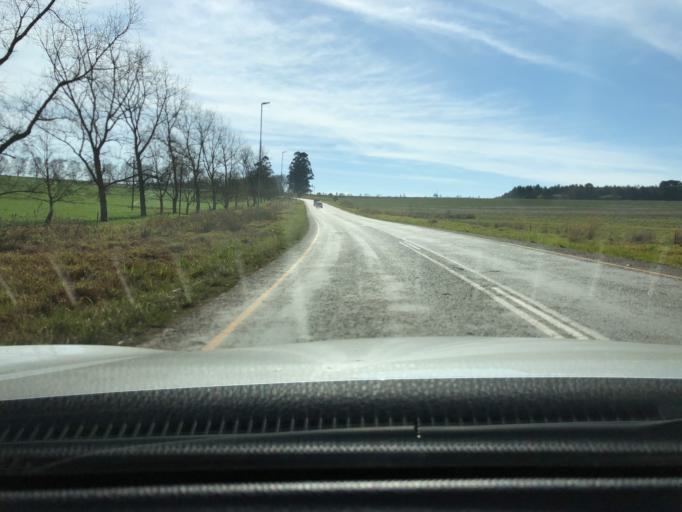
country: ZA
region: KwaZulu-Natal
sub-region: Sisonke District Municipality
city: Ixopo
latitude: -30.1414
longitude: 30.0773
